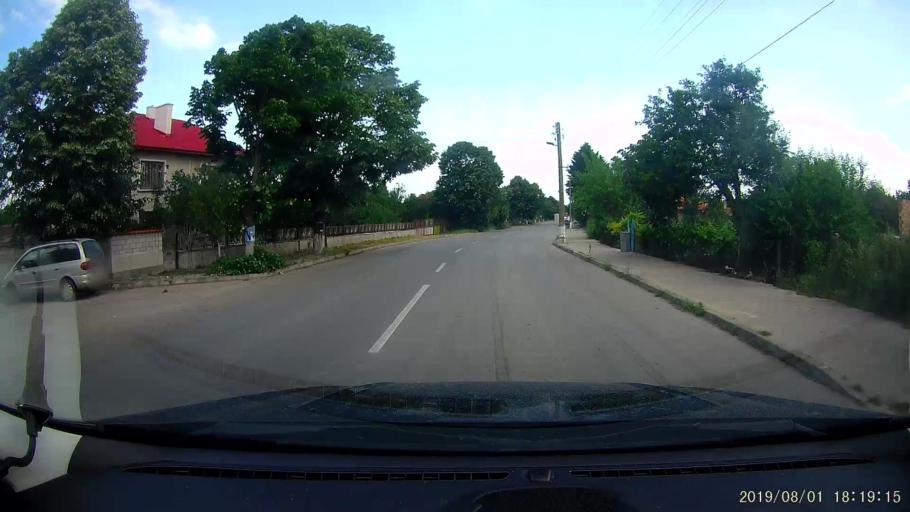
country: BG
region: Shumen
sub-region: Obshtina Kaolinovo
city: Kaolinovo
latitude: 43.6860
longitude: 27.0896
